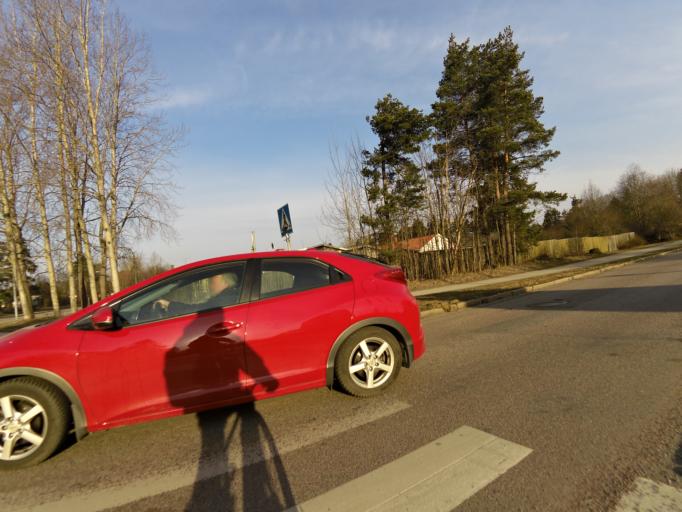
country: SE
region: Gaevleborg
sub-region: Gavle Kommun
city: Gavle
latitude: 60.6575
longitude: 17.1331
